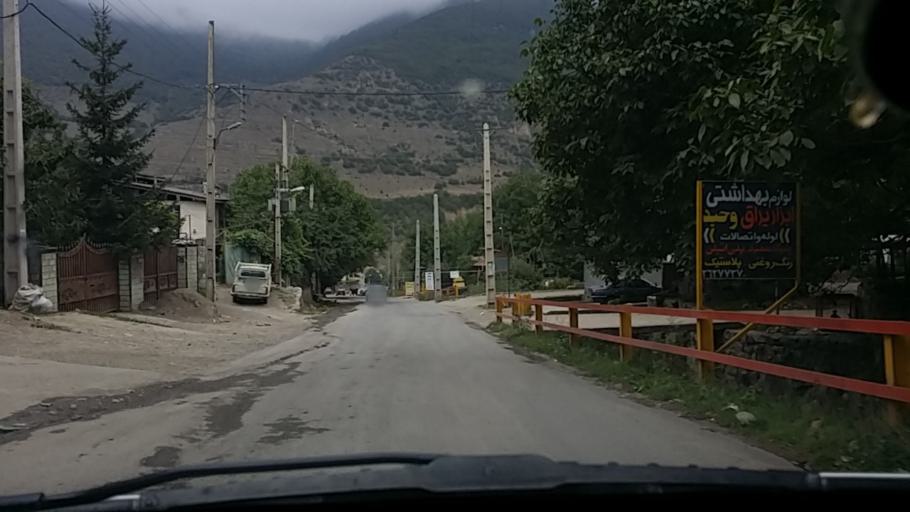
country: IR
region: Mazandaran
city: `Abbasabad
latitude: 36.4845
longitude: 51.1348
